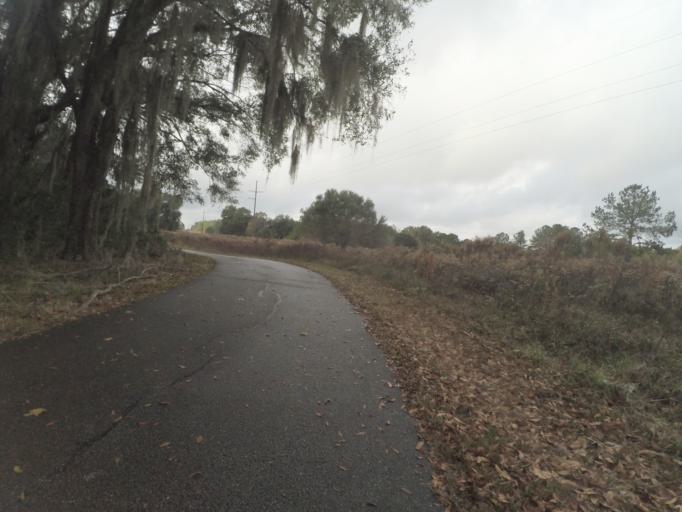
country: US
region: Florida
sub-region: Alachua County
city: Gainesville
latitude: 29.6081
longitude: -82.2871
